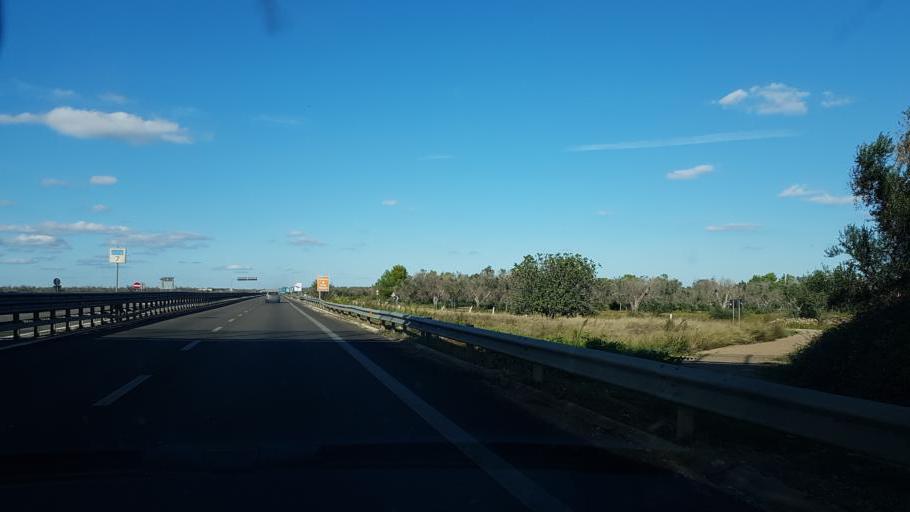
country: IT
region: Apulia
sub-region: Provincia di Lecce
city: San Pietro in Lama
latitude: 40.2577
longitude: 18.1188
